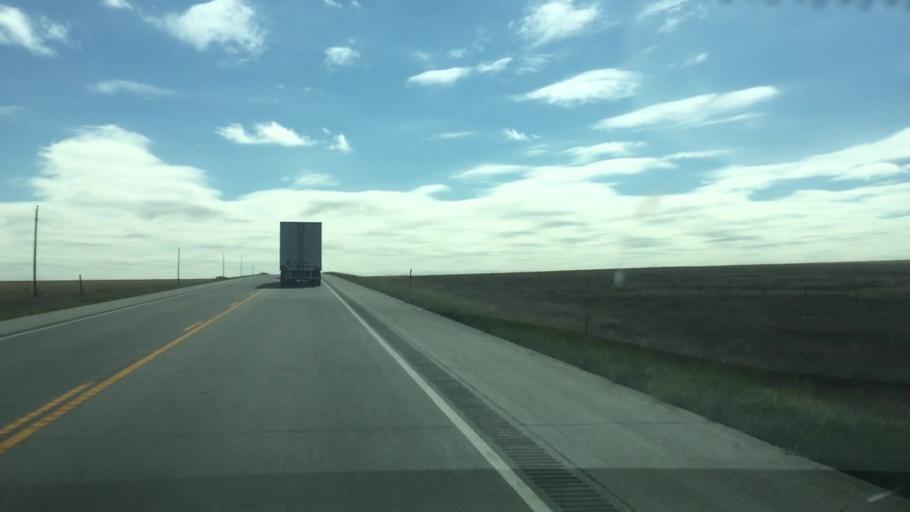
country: US
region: Colorado
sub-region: Lincoln County
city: Hugo
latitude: 39.0256
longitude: -103.3178
